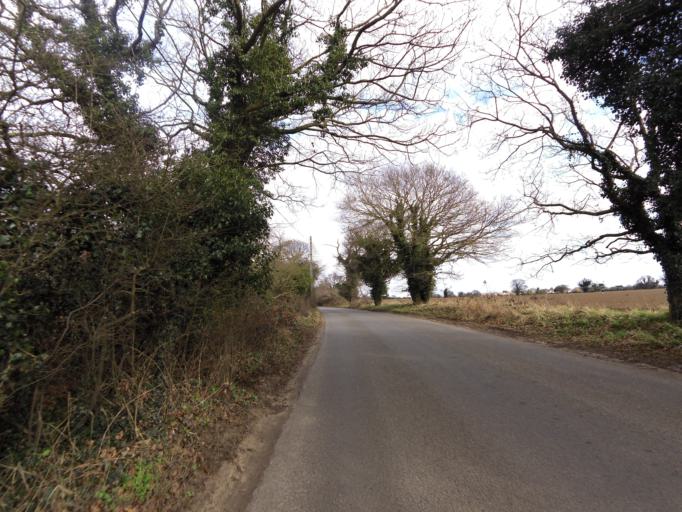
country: GB
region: England
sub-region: Suffolk
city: Woodbridge
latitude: 52.0544
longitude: 1.3078
